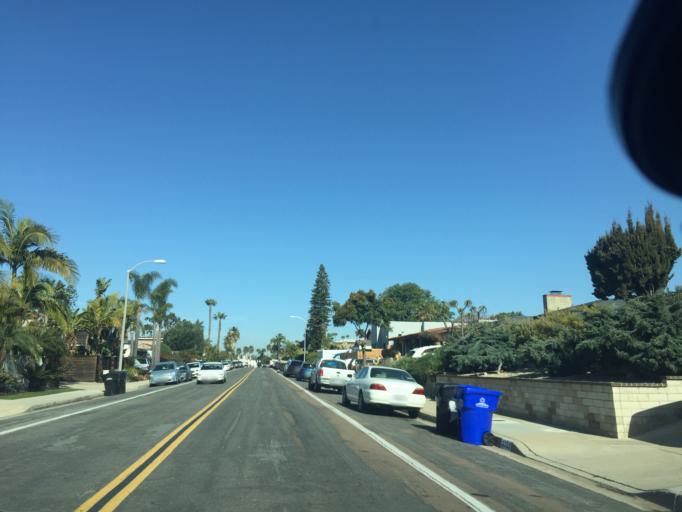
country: US
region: California
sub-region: San Diego County
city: San Diego
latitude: 32.7913
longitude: -117.1927
